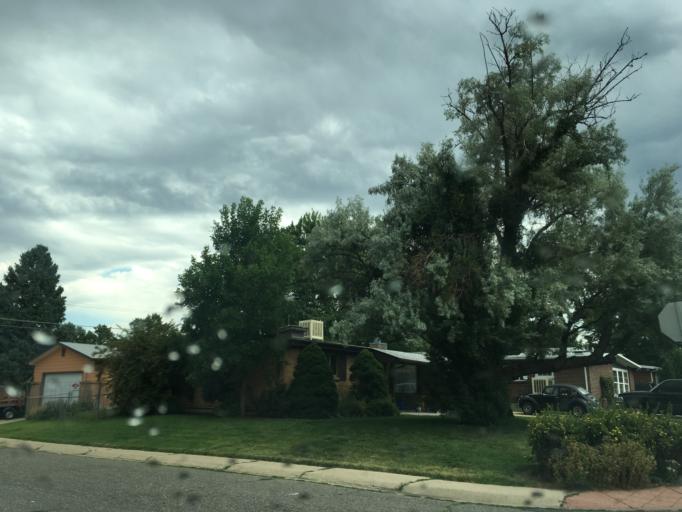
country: US
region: Colorado
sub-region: Arapahoe County
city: Sheridan
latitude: 39.6704
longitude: -105.0397
